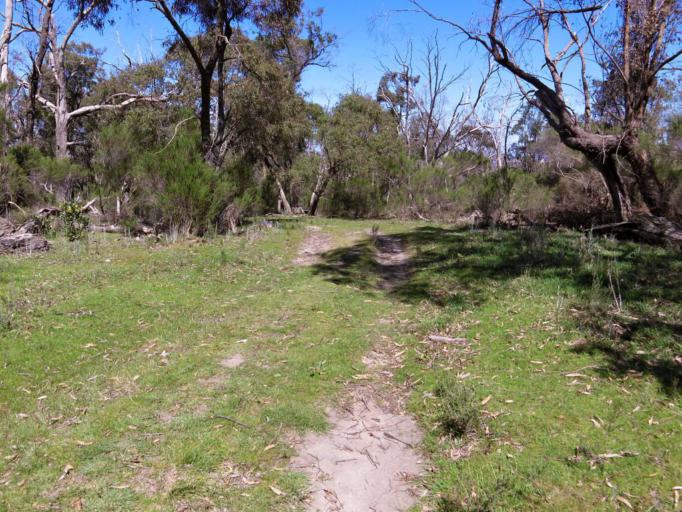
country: AU
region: Victoria
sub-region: Casey
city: Endeavour Hills
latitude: -37.9483
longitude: 145.2669
